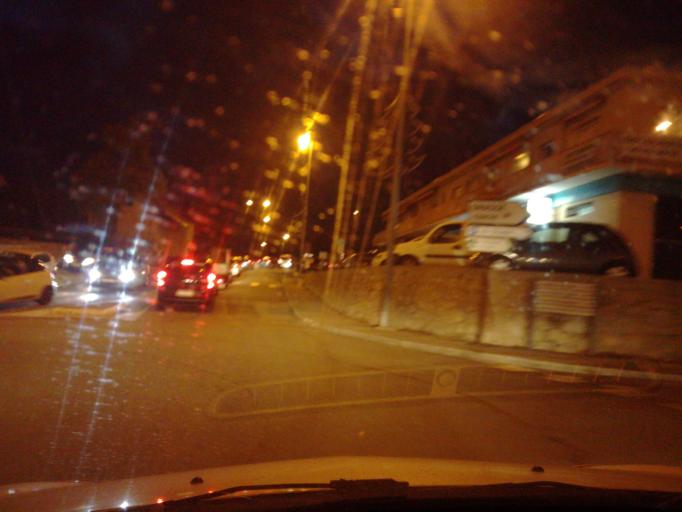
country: FR
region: Provence-Alpes-Cote d'Azur
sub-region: Departement des Alpes-Maritimes
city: Grasse
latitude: 43.6409
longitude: 6.9117
